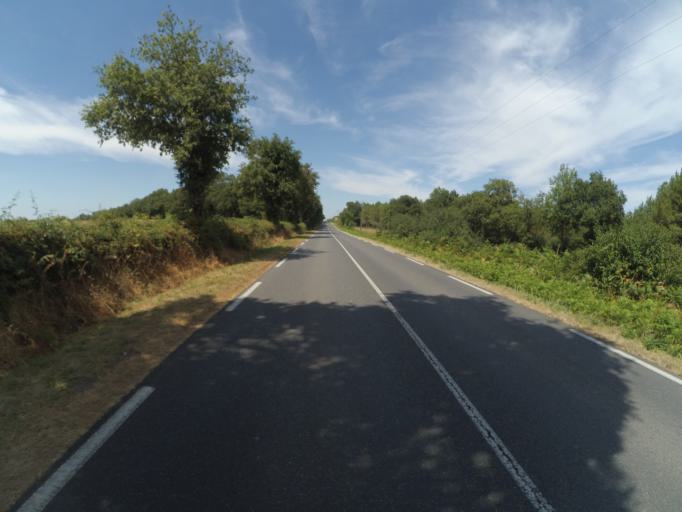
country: FR
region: Poitou-Charentes
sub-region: Departement de la Vienne
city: Availles-Limouzine
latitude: 46.0911
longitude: 0.5850
